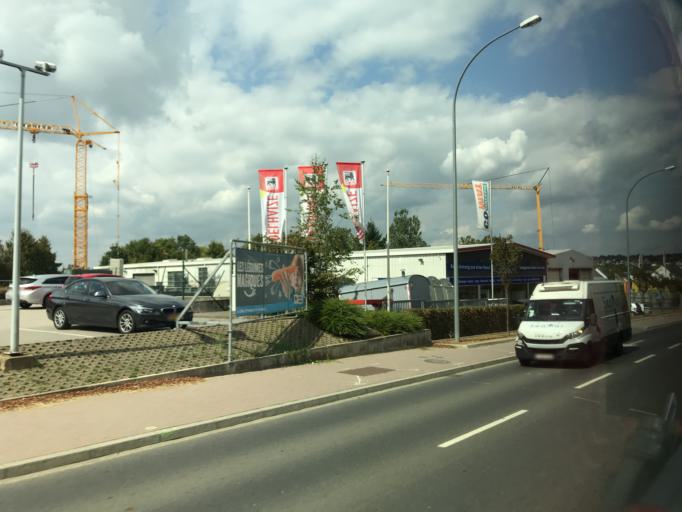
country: LU
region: Luxembourg
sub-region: Canton de Luxembourg
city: Alzingen
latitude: 49.5618
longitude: 6.1651
